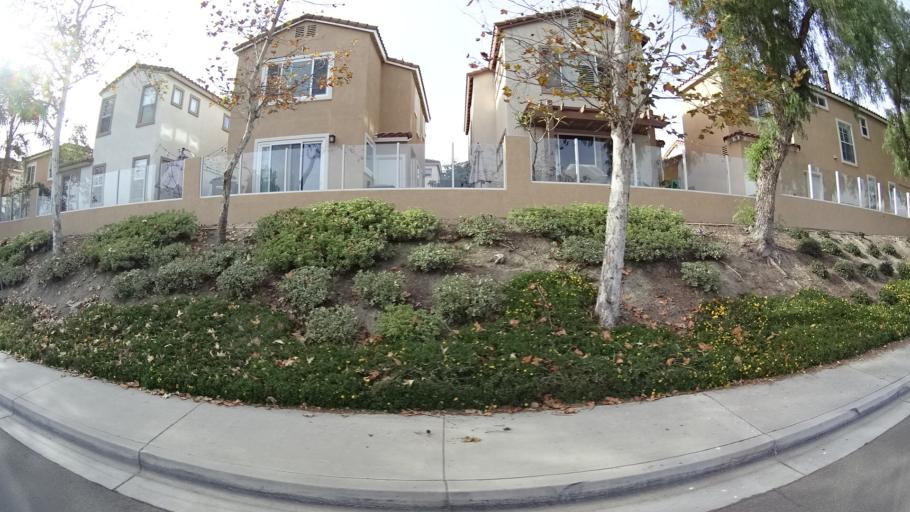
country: US
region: California
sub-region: Orange County
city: Aliso Viejo
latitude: 33.5543
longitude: -117.7218
